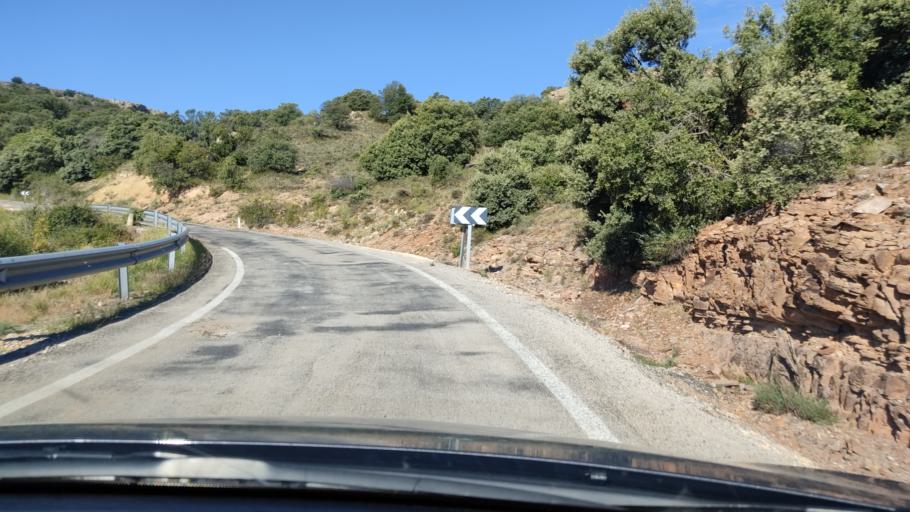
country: ES
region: Aragon
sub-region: Provincia de Teruel
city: Anadon
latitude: 41.0063
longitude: -1.0031
